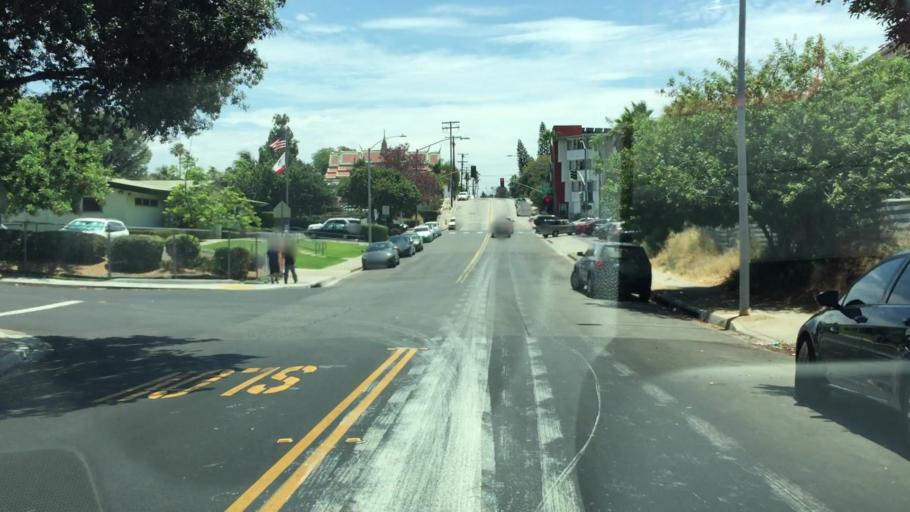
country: US
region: California
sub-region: San Diego County
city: Lemon Grove
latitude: 32.7502
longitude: -117.0836
